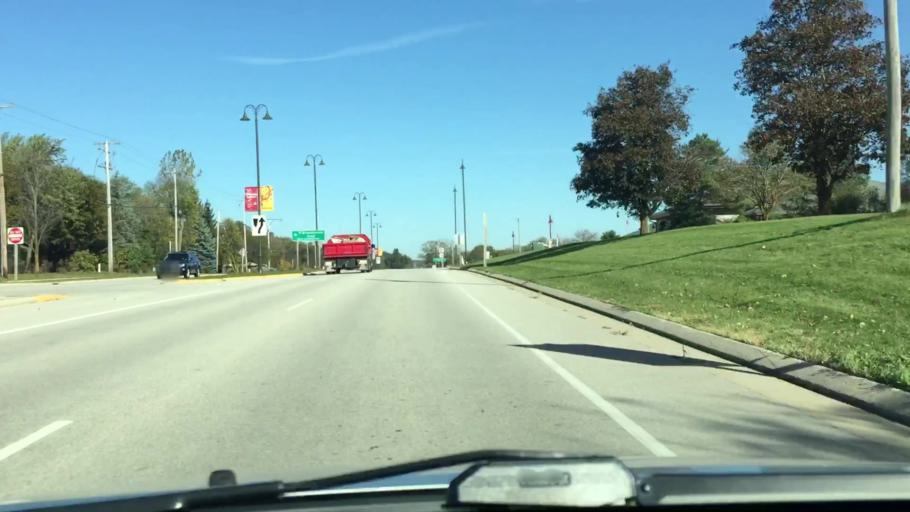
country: US
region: Wisconsin
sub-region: Waukesha County
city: Wales
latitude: 42.9930
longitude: -88.3842
